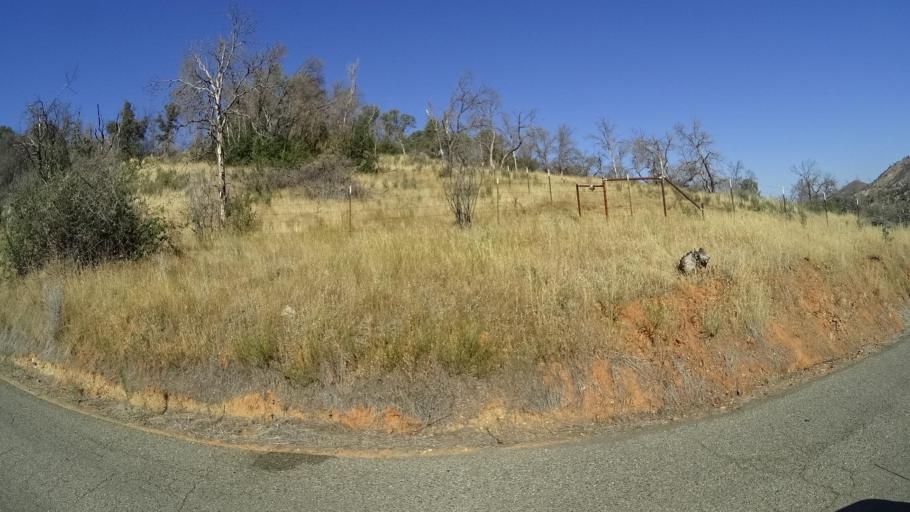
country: US
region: California
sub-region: Mariposa County
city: Mariposa
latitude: 37.5746
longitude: -120.1714
